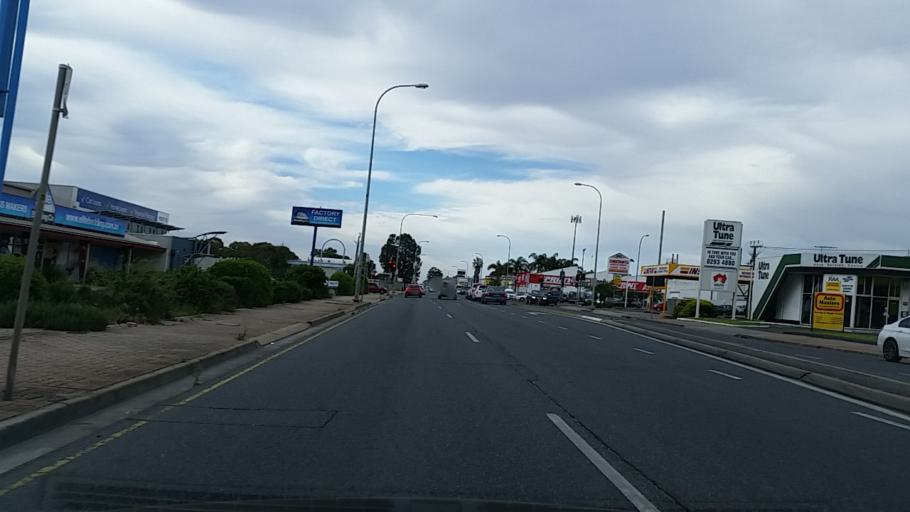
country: AU
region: South Australia
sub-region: Mitcham
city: Clarence Gardens
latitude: -34.9791
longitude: 138.5737
